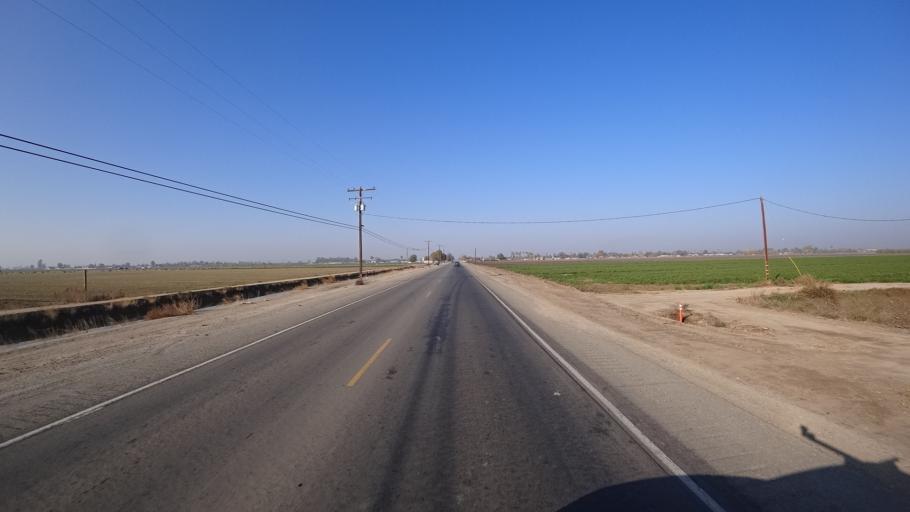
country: US
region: California
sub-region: Kern County
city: Greenfield
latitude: 35.2669
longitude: -118.9922
